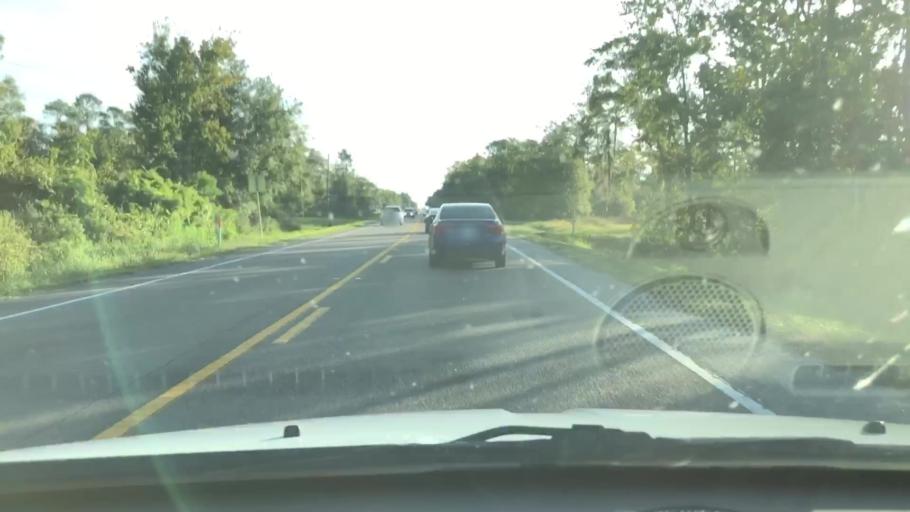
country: US
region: Florida
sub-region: Osceola County
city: Campbell
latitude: 28.2548
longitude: -81.4779
